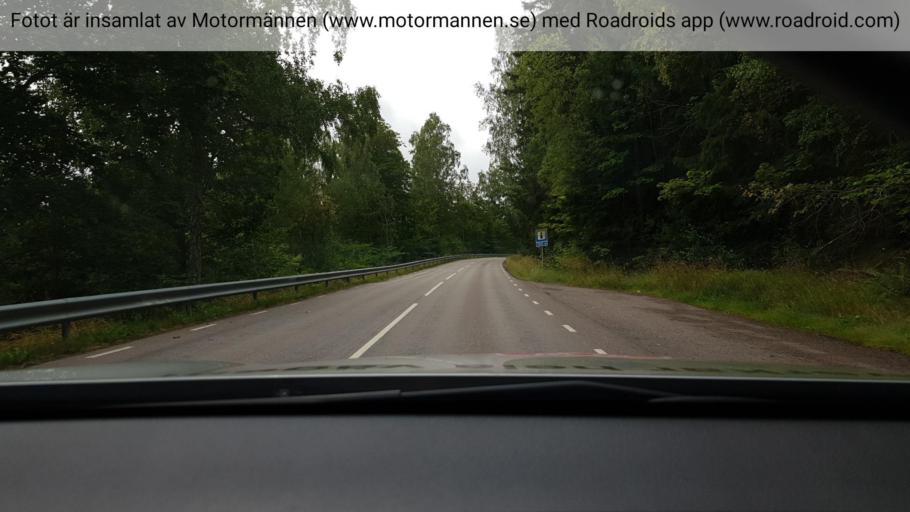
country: SE
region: Soedermanland
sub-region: Gnesta Kommun
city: Gnesta
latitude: 59.0612
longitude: 17.3018
